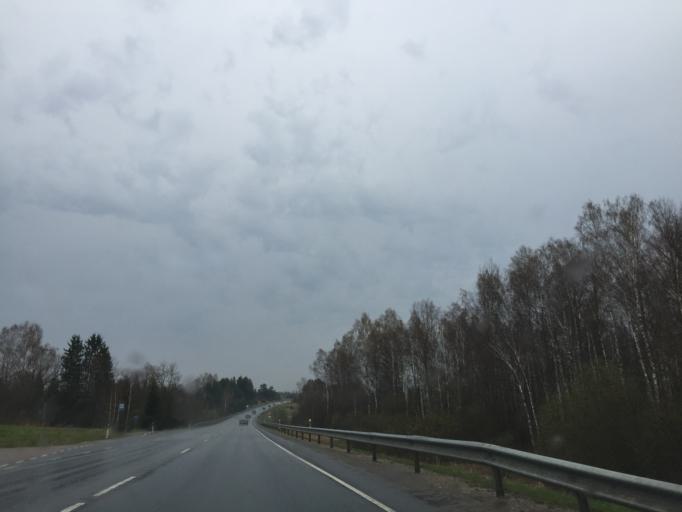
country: EE
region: Tartu
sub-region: UElenurme vald
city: Ulenurme
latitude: 58.2518
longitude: 26.6794
